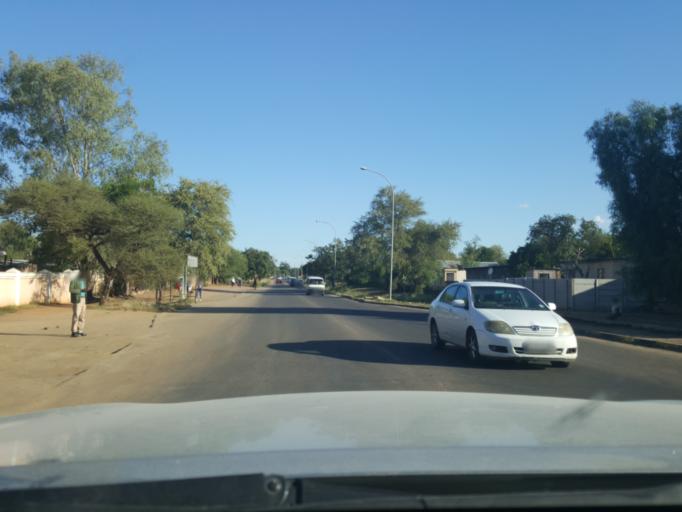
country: BW
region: South East
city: Gaborone
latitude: -24.6222
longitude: 25.9435
